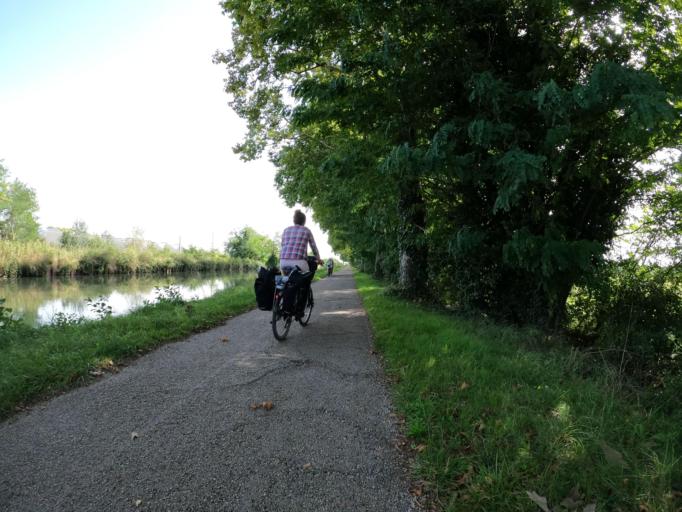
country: FR
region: Midi-Pyrenees
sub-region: Departement de la Haute-Garonne
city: Saint-Jory
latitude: 43.7507
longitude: 1.3624
